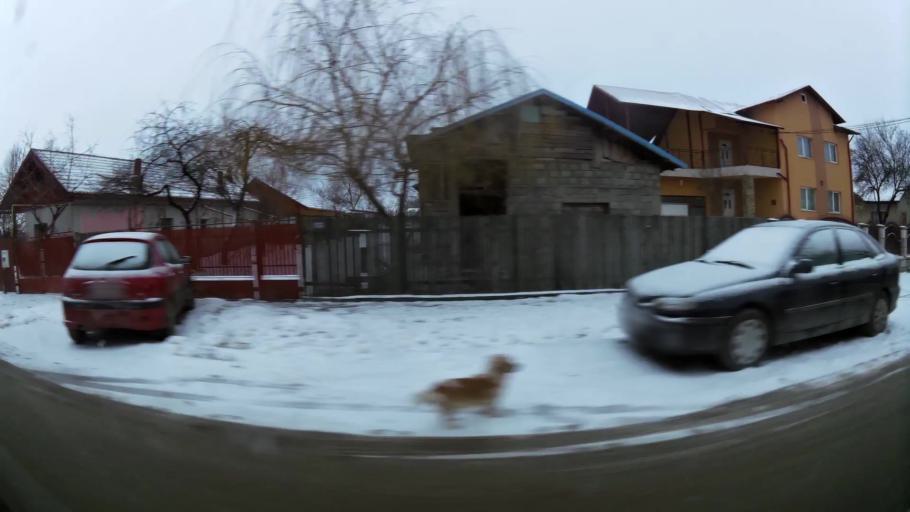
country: RO
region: Prahova
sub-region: Comuna Berceni
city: Corlatesti
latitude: 44.9136
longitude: 26.0850
